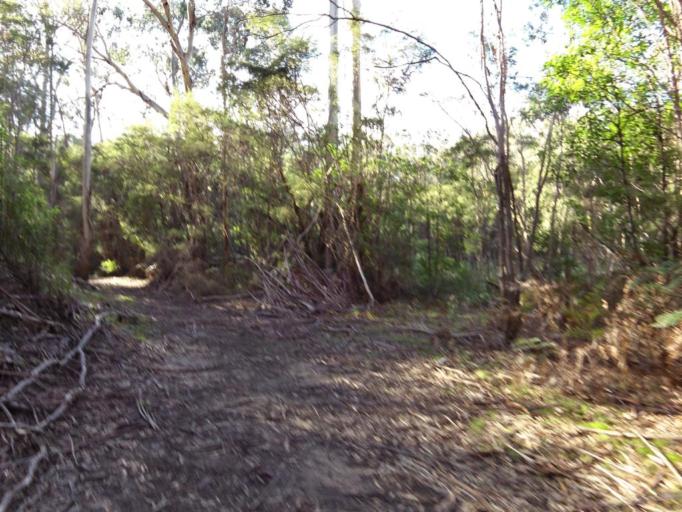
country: AU
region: Victoria
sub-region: Yarra Ranges
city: Chirnside Park
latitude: -37.7156
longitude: 145.2827
